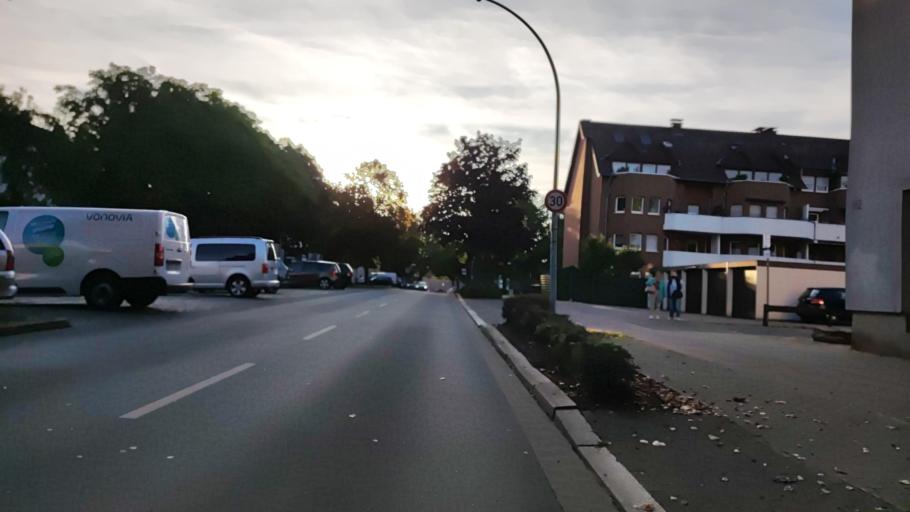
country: DE
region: North Rhine-Westphalia
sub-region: Regierungsbezirk Arnsberg
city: Herne
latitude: 51.5393
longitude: 7.2450
